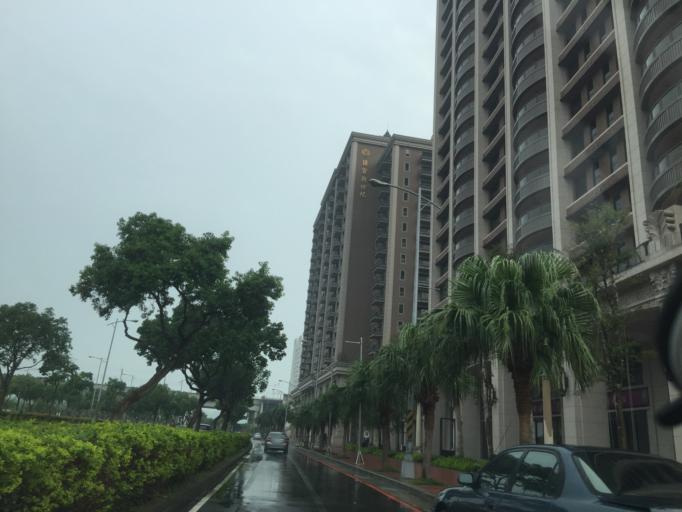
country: TW
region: Taiwan
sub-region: Hsinchu
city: Zhubei
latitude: 24.8112
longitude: 121.0378
